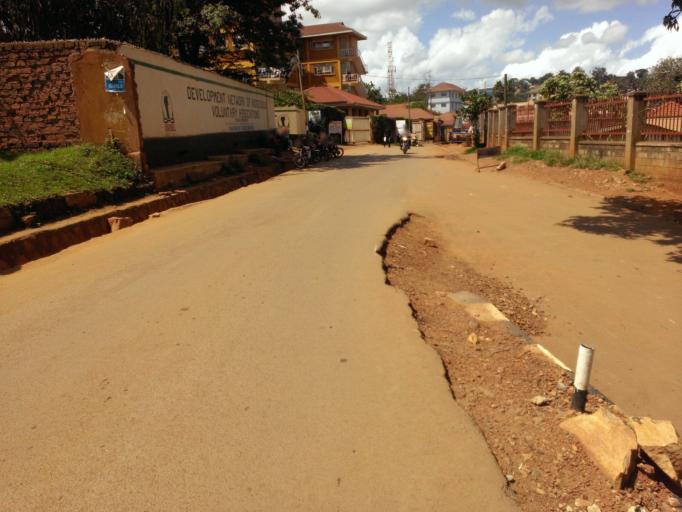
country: UG
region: Central Region
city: Kampala Central Division
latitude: 0.3257
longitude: 32.5688
